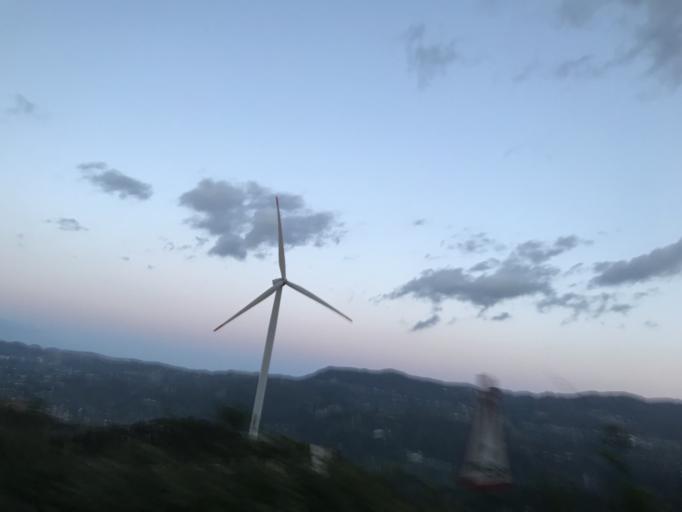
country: TR
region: Hatay
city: Buyukcat
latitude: 36.0972
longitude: 36.0417
